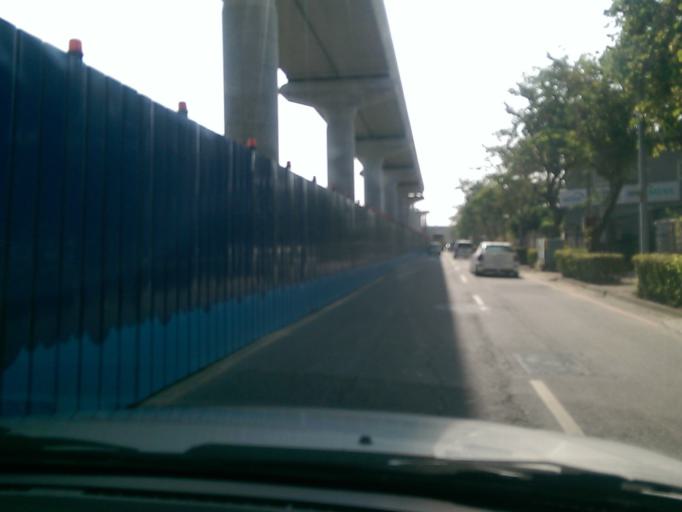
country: TW
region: Taiwan
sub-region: Taichung City
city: Taichung
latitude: 24.1179
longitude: 120.6454
